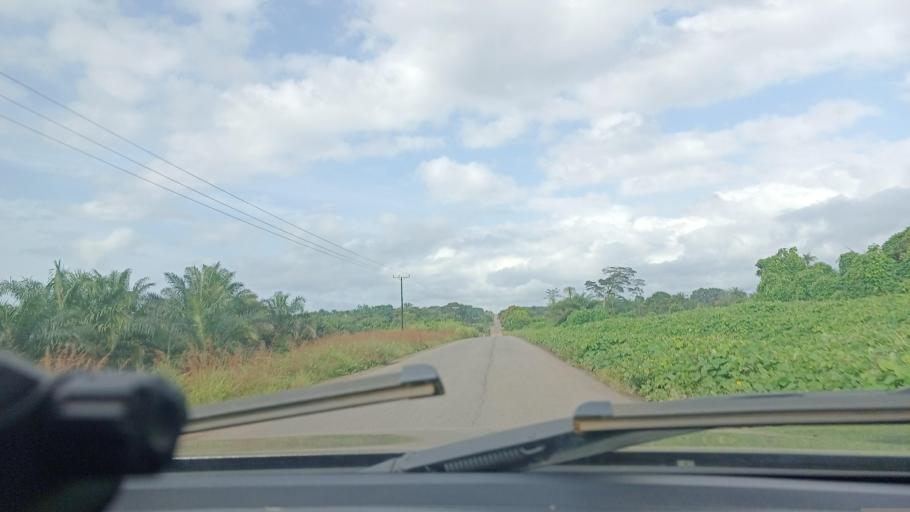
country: LR
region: Bomi
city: Tubmanburg
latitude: 6.7294
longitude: -11.0189
